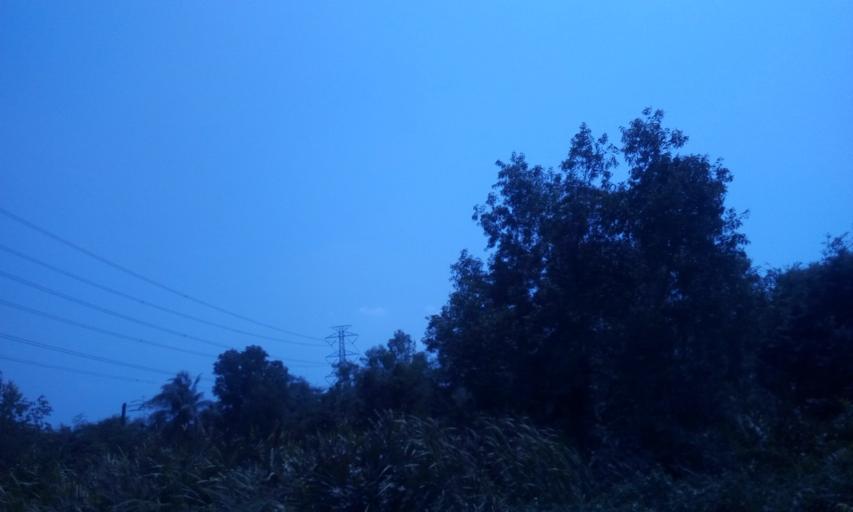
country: TH
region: Chachoengsao
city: Bang Nam Priao
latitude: 13.9052
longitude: 100.9729
